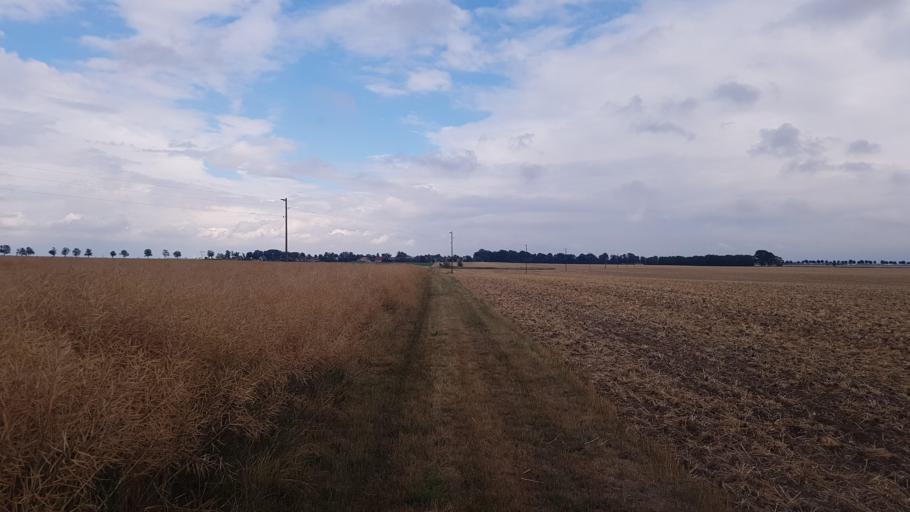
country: DE
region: Brandenburg
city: Juterbog
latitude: 51.9362
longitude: 13.1026
